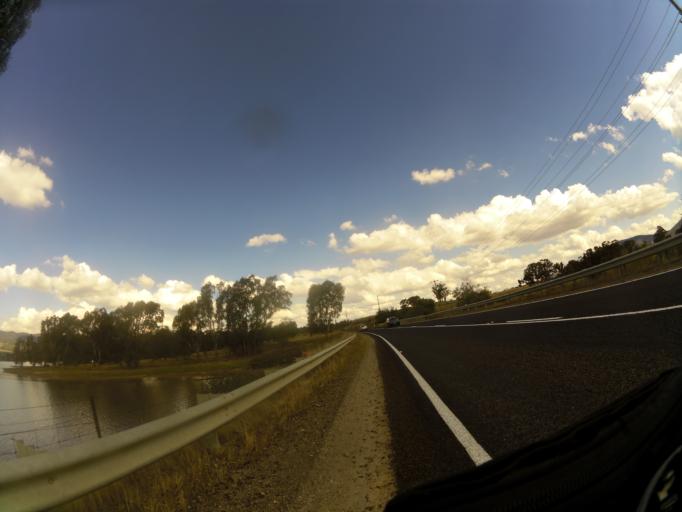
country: AU
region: Victoria
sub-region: Mansfield
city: Mansfield
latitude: -36.9051
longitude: 145.9968
